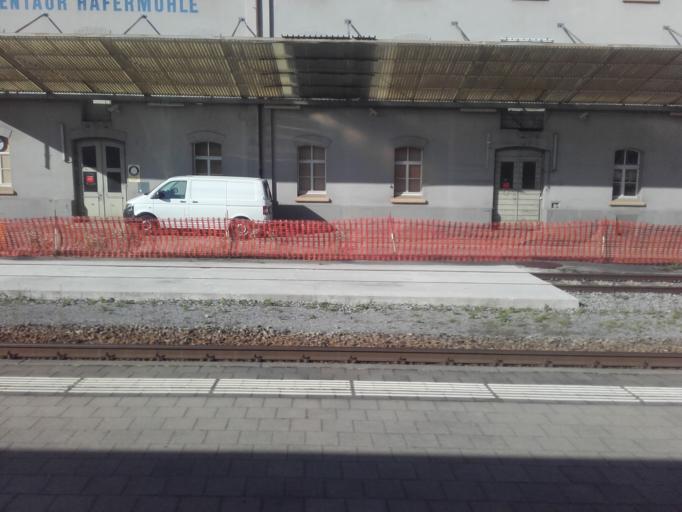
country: CH
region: Bern
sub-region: Emmental District
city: Lutzelfluh
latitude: 47.0048
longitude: 7.6834
